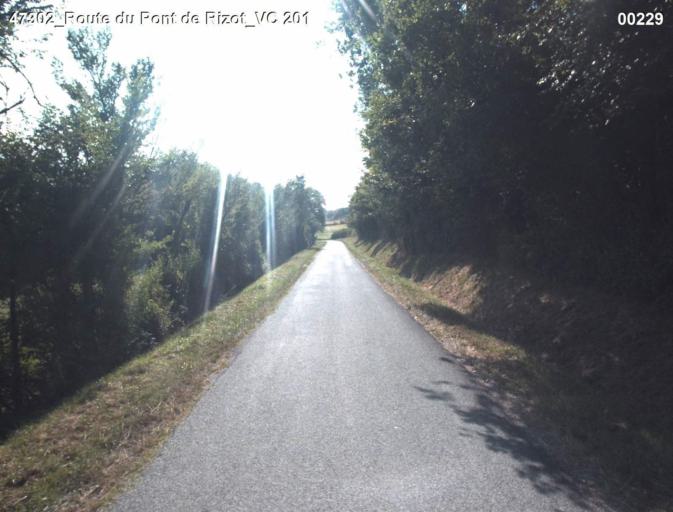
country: FR
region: Aquitaine
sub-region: Departement du Lot-et-Garonne
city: Mezin
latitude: 44.0406
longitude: 0.1973
